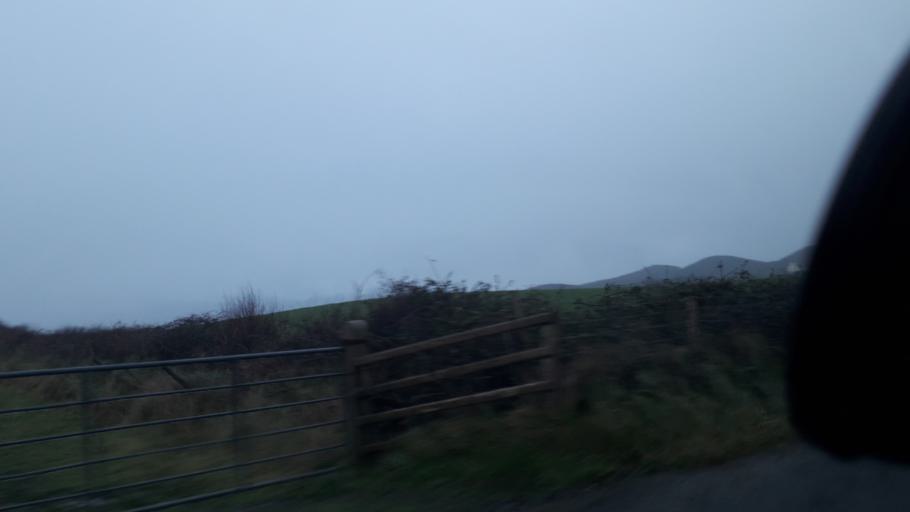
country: IE
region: Ulster
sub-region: County Donegal
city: Buncrana
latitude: 55.2733
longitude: -7.6386
